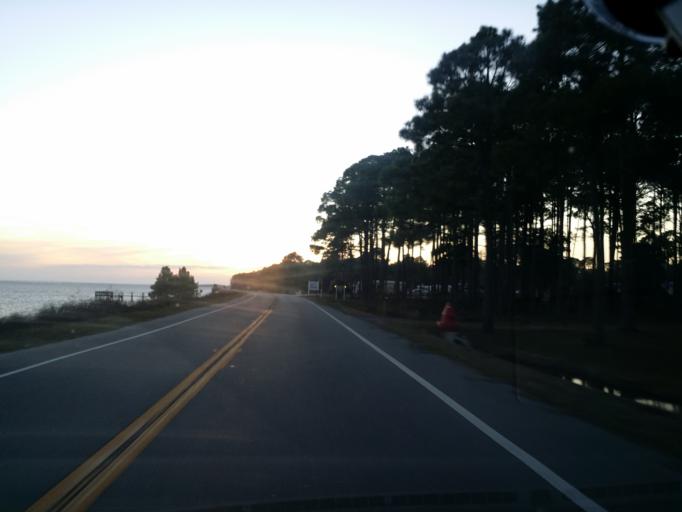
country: US
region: Florida
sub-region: Franklin County
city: Eastpoint
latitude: 29.7567
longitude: -84.8362
